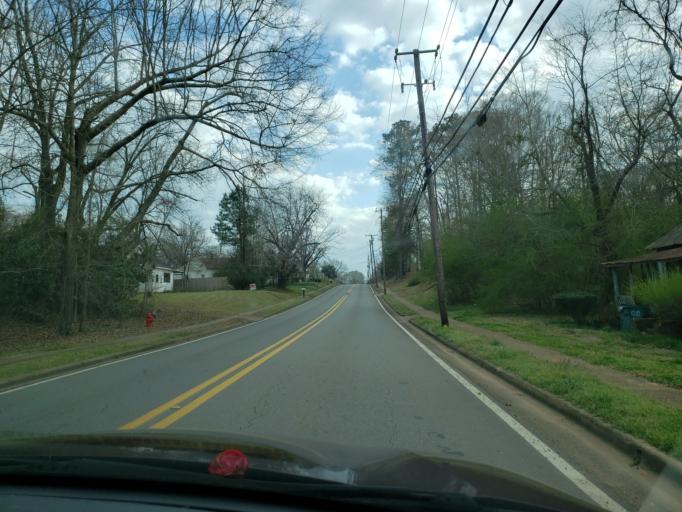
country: US
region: Alabama
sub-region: Hale County
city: Greensboro
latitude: 32.7084
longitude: -87.5922
